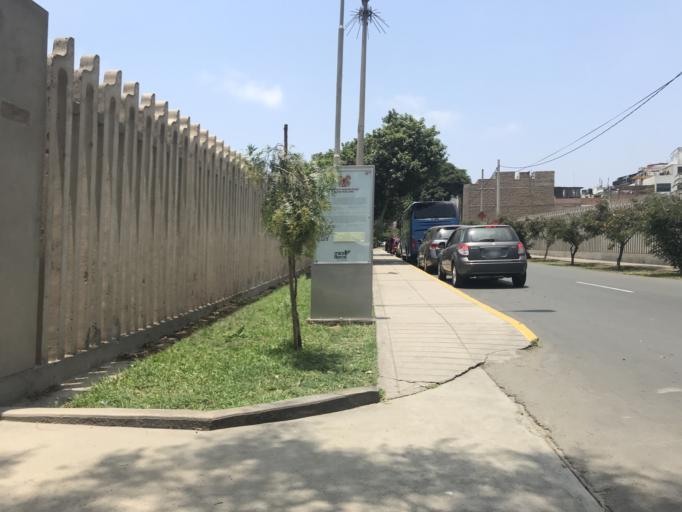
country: PE
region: Lima
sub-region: Lima
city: San Isidro
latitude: -12.1106
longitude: -77.0324
